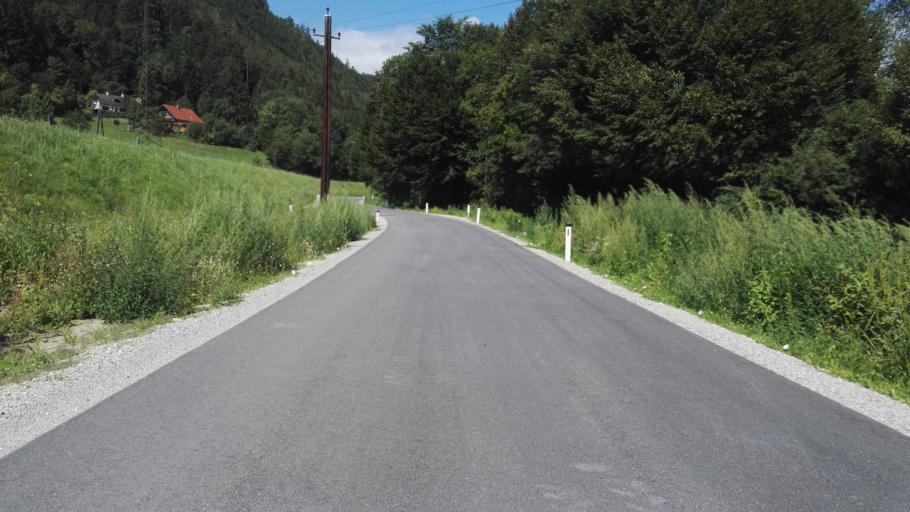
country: AT
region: Styria
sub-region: Politischer Bezirk Graz-Umgebung
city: Peggau
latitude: 47.2276
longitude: 15.3290
